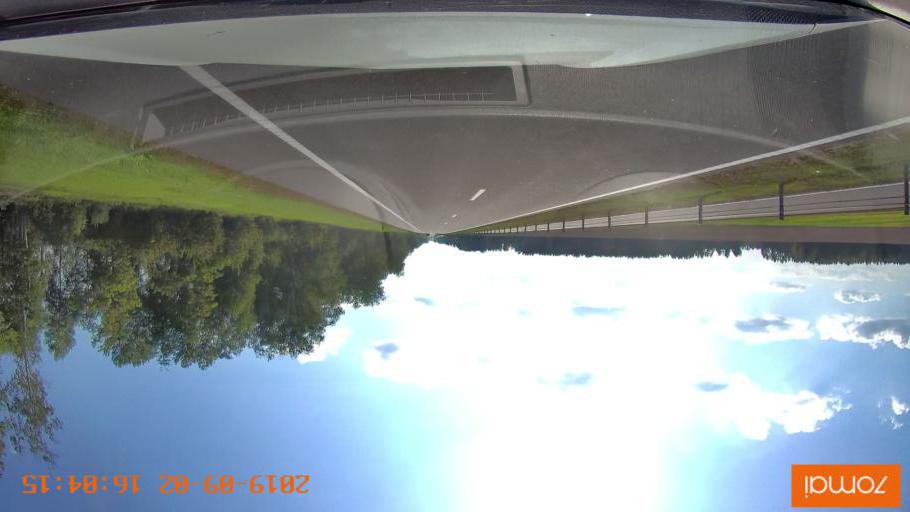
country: BY
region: Minsk
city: Byerazino
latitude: 53.7998
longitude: 28.8478
